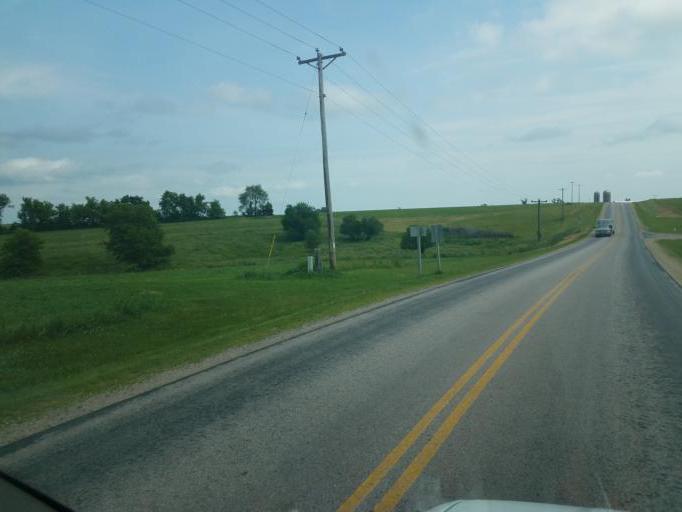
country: US
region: Wisconsin
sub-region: Monroe County
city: Cashton
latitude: 43.7490
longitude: -90.7716
